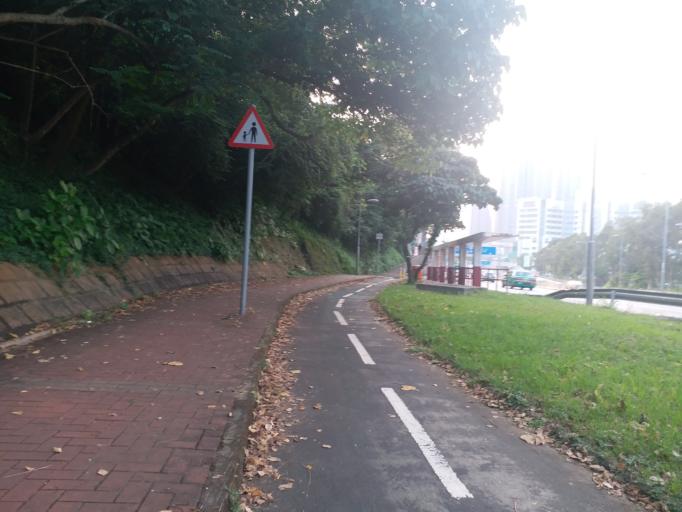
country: HK
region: Yuen Long
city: Yuen Long Kau Hui
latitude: 22.4439
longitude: 114.0463
